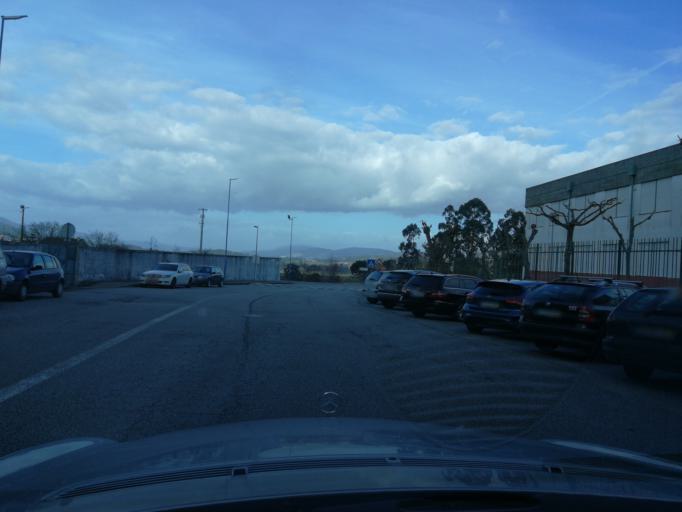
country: PT
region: Viana do Castelo
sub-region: Valenca
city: Valenca
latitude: 42.0302
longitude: -8.6393
